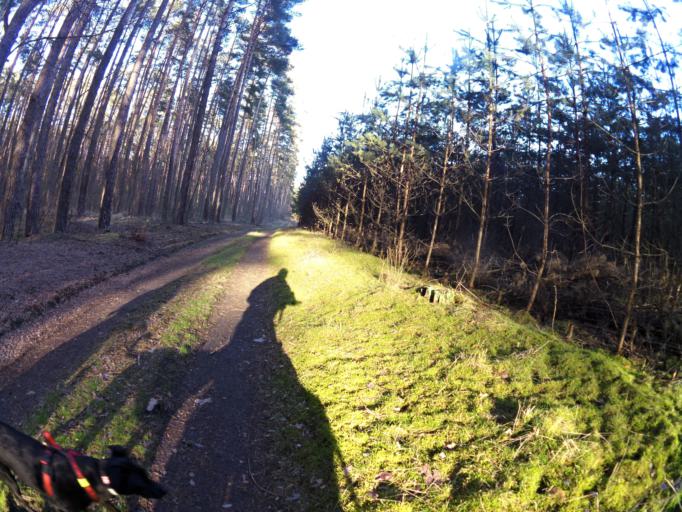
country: PL
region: West Pomeranian Voivodeship
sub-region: Powiat mysliborski
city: Debno
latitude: 52.8227
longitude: 14.7461
